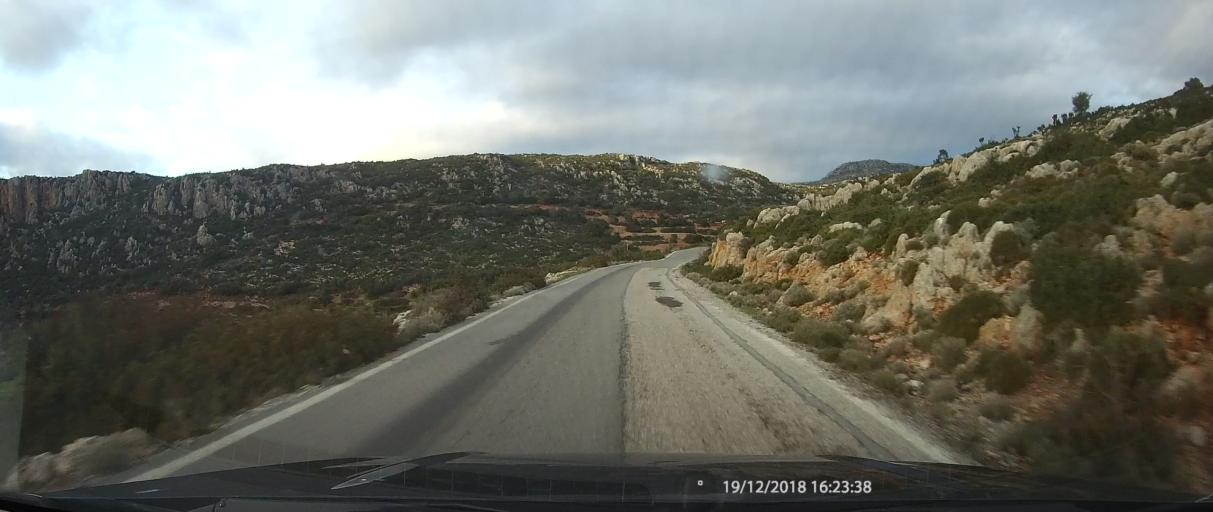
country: GR
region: Peloponnese
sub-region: Nomos Lakonias
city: Kato Glikovrisi
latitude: 36.9456
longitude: 22.8352
